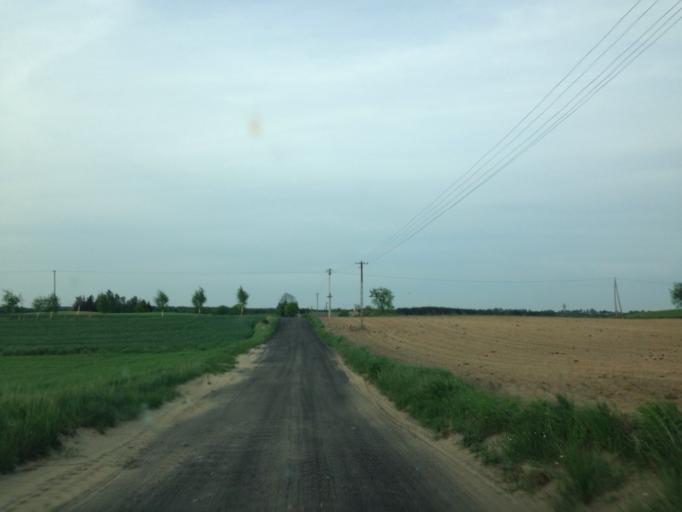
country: PL
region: Kujawsko-Pomorskie
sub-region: Powiat brodnicki
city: Brodnica
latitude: 53.3063
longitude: 19.3529
